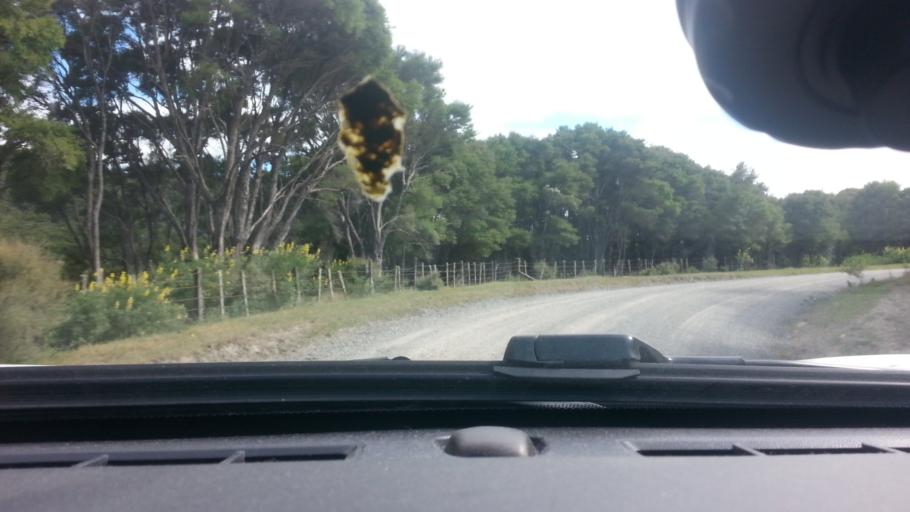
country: NZ
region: Wellington
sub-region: South Wairarapa District
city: Waipawa
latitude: -41.4957
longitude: 175.4364
